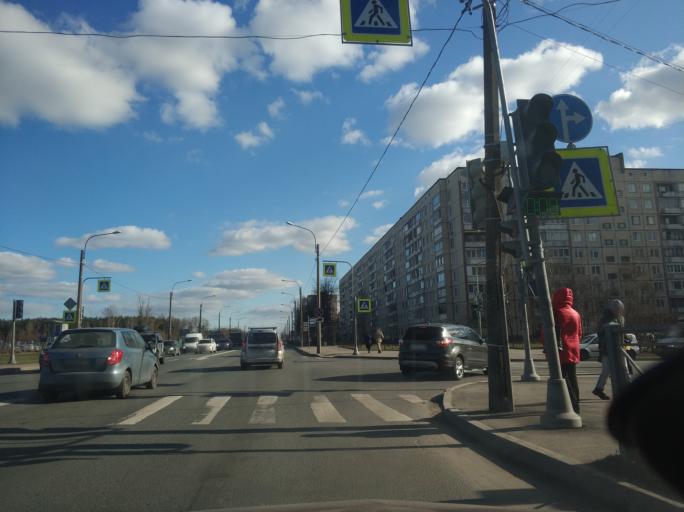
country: RU
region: St.-Petersburg
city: Krasnogvargeisky
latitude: 59.9536
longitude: 30.4971
